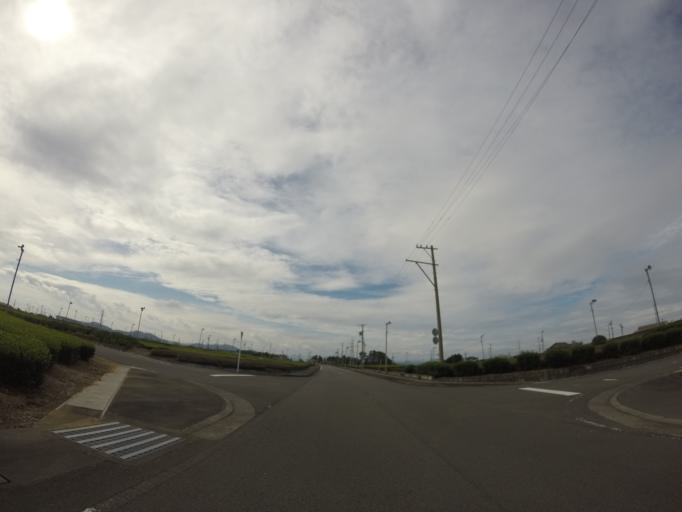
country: JP
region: Shizuoka
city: Kanaya
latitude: 34.8014
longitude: 138.1405
